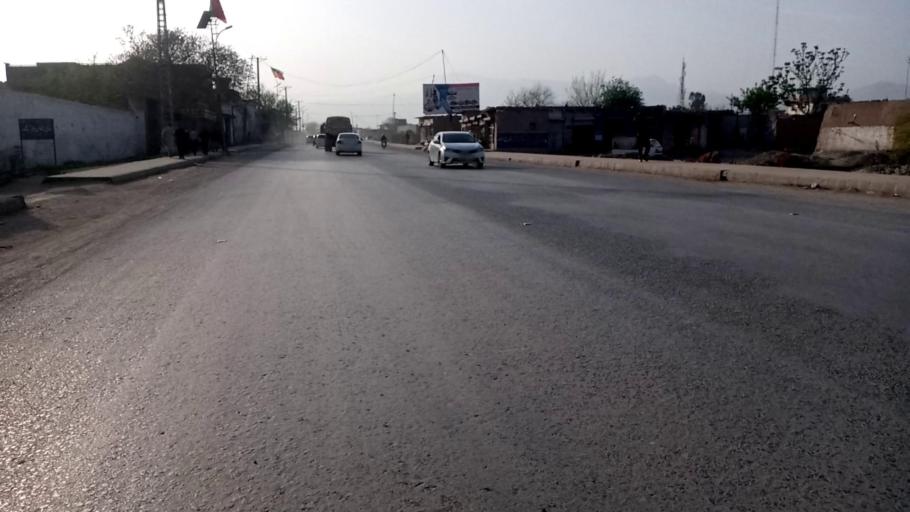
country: PK
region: Khyber Pakhtunkhwa
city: Peshawar
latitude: 33.9990
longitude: 71.4161
